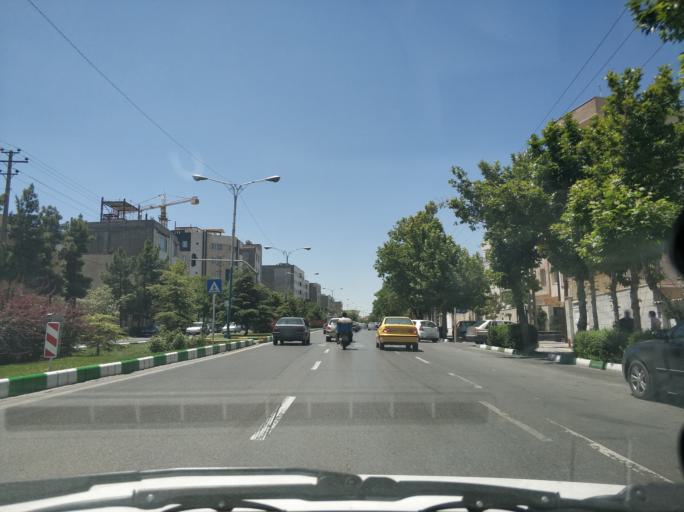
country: IR
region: Razavi Khorasan
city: Mashhad
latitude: 36.3119
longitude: 59.4956
